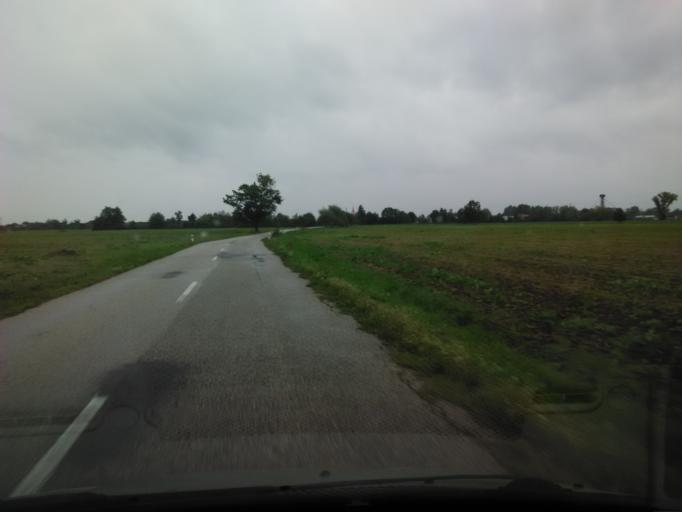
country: SK
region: Nitriansky
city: Tlmace
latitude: 48.2784
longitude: 18.5313
